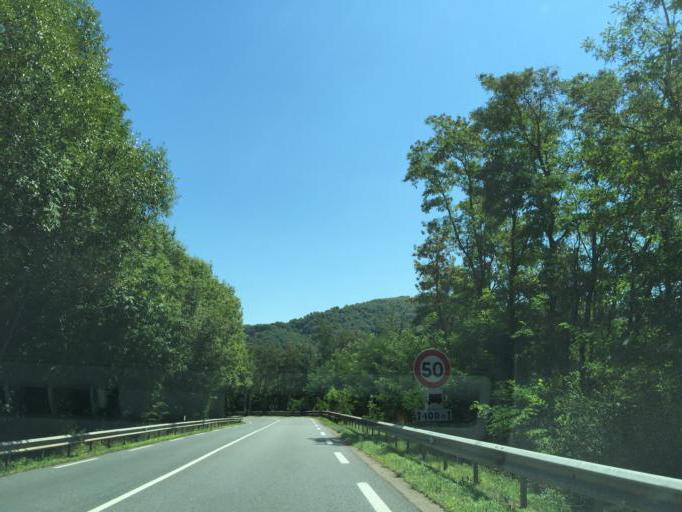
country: FR
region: Midi-Pyrenees
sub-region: Departement de l'Aveyron
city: Espalion
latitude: 44.5143
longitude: 2.7520
